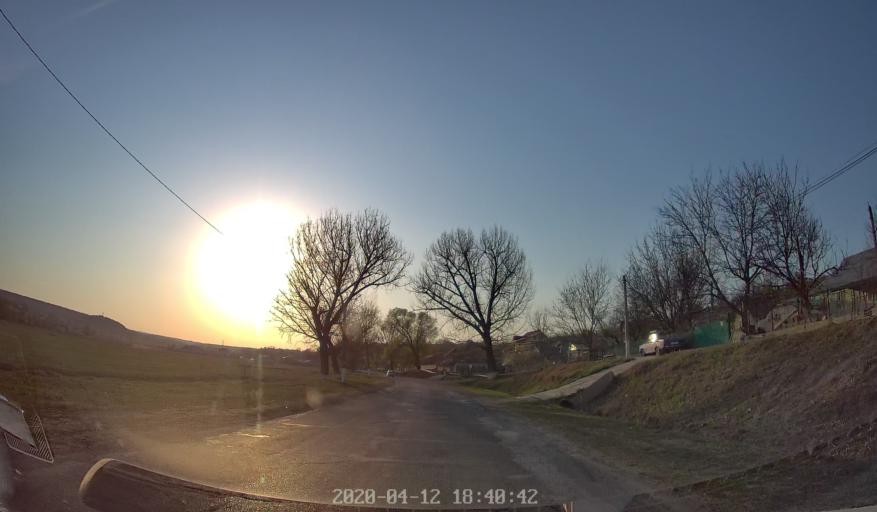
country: MD
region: Chisinau
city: Ciorescu
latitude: 47.1349
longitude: 28.9634
